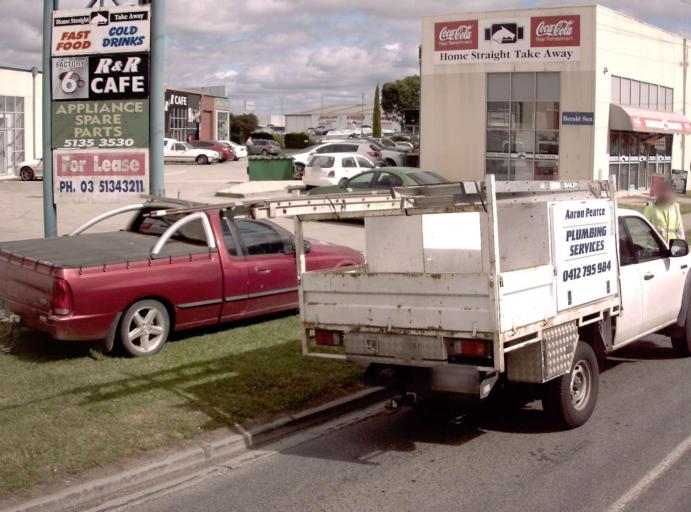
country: AU
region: Victoria
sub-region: Latrobe
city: Morwell
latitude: -38.2311
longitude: 146.4415
